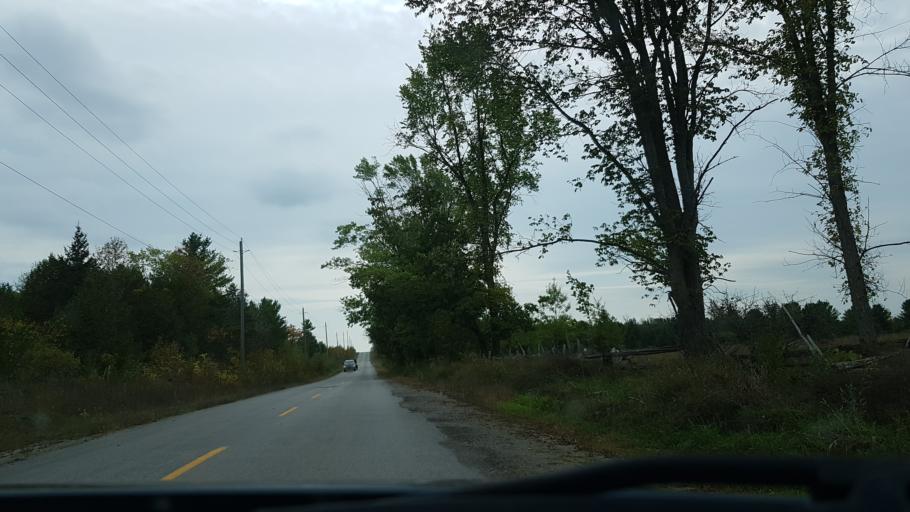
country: CA
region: Ontario
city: Orillia
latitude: 44.6578
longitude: -78.9684
